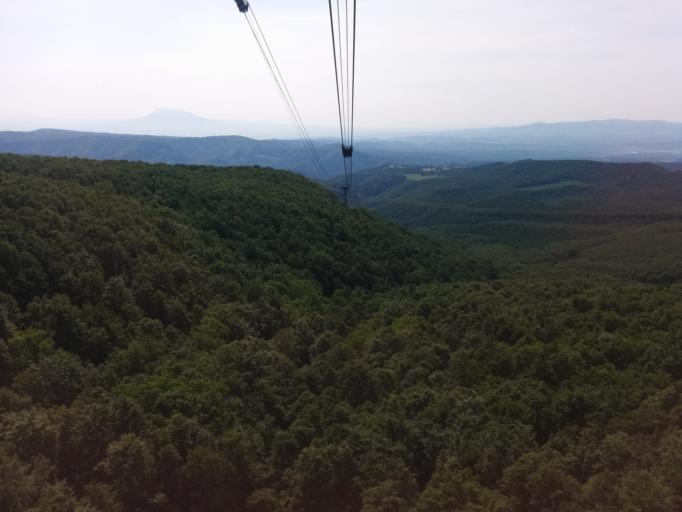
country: JP
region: Aomori
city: Aomori Shi
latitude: 40.6789
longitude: 140.8430
